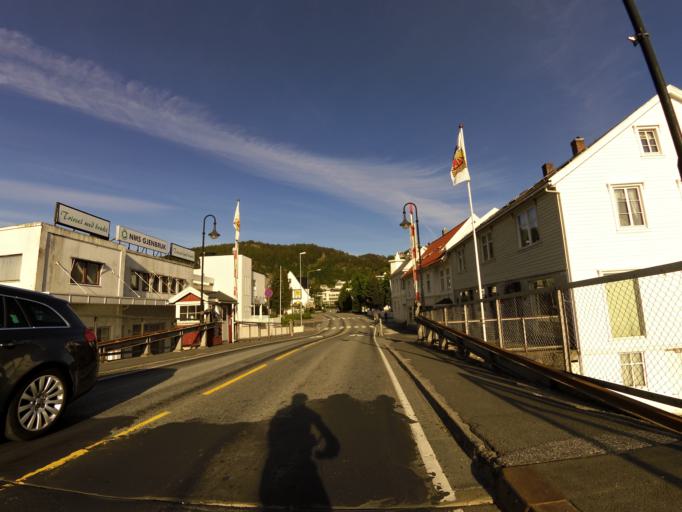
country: NO
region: Vest-Agder
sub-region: Flekkefjord
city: Flekkefjord
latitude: 58.2963
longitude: 6.6636
